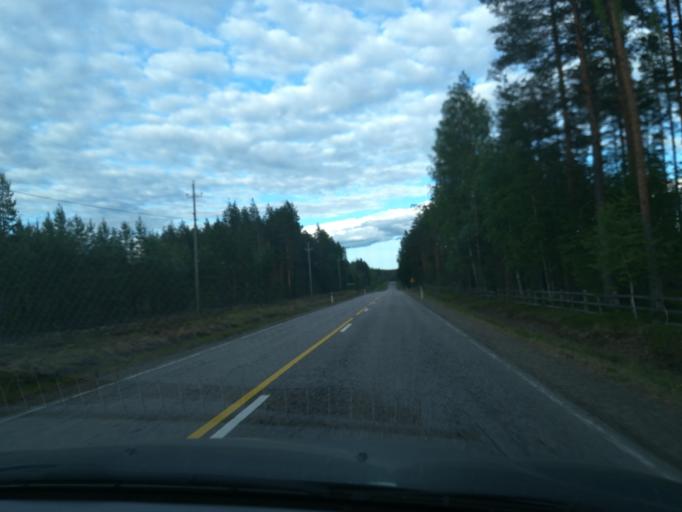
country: FI
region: Southern Savonia
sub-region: Mikkeli
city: Puumala
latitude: 61.5603
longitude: 28.0116
